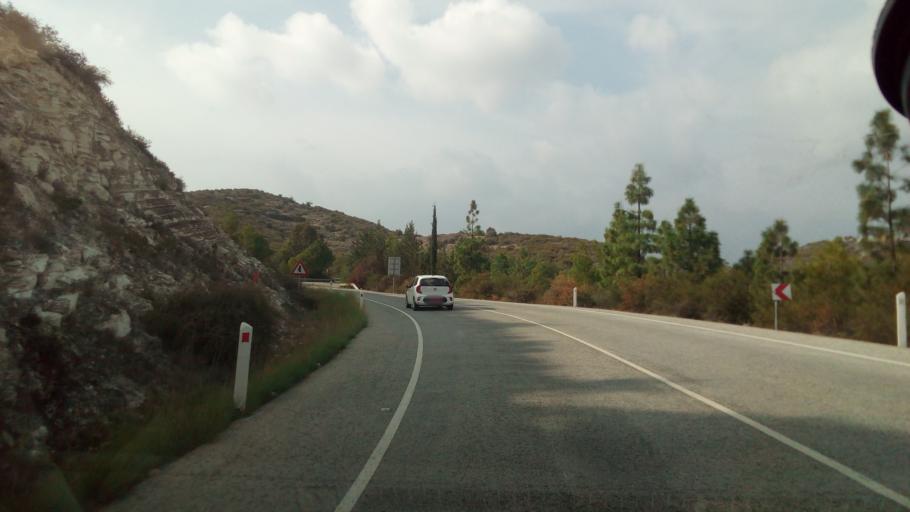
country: CY
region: Larnaka
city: Kofinou
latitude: 34.8251
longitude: 33.3632
